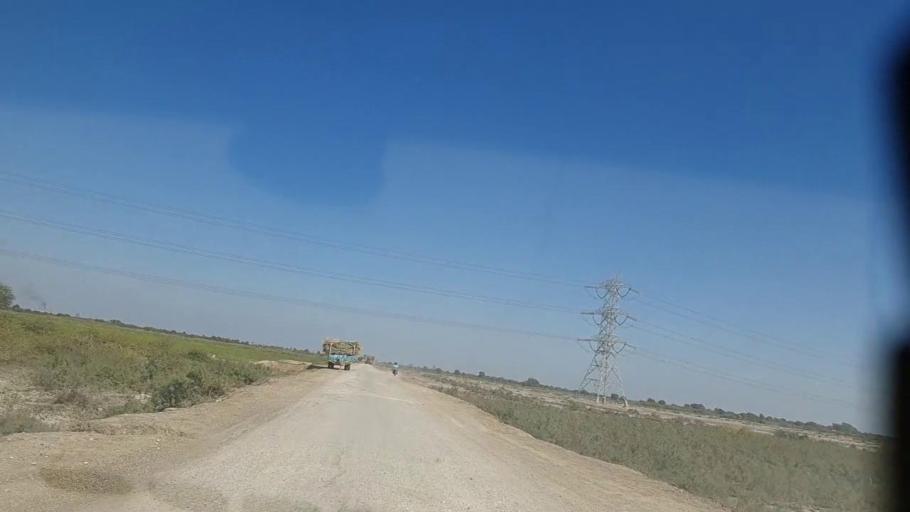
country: PK
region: Sindh
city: Mirwah Gorchani
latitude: 25.2598
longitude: 69.0494
